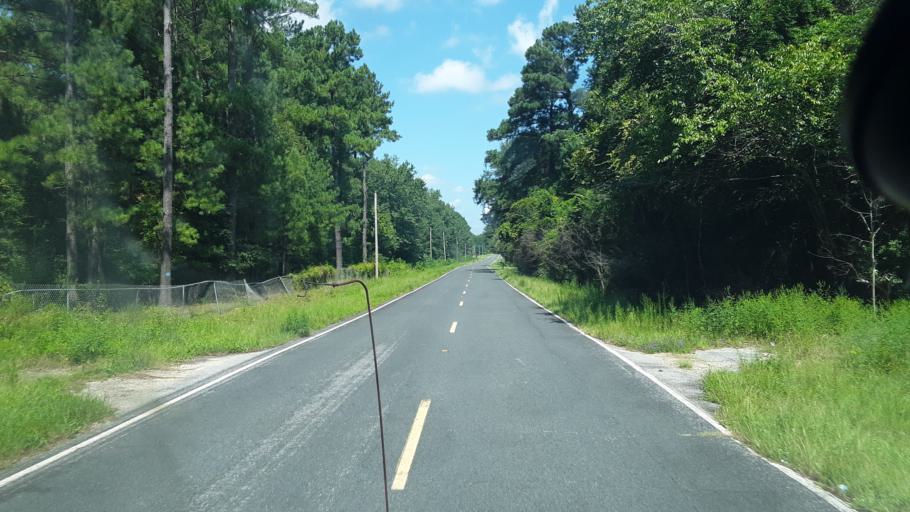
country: US
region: South Carolina
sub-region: Bamberg County
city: Bamberg
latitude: 33.3616
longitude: -81.0148
